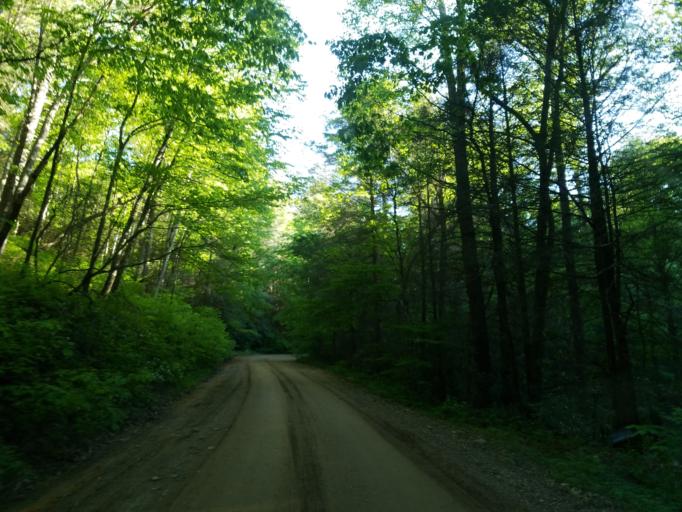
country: US
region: Georgia
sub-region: Lumpkin County
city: Dahlonega
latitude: 34.6971
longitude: -84.1417
